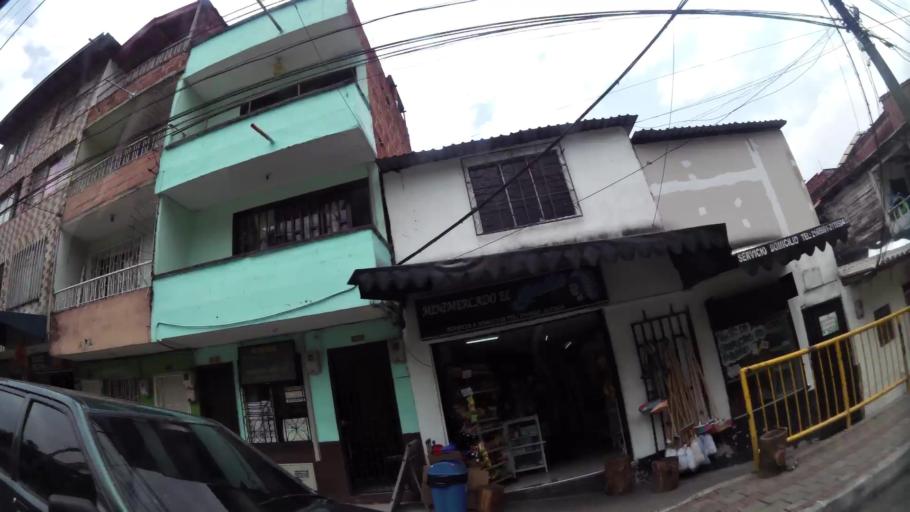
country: CO
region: Antioquia
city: Medellin
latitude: 6.2344
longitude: -75.5640
